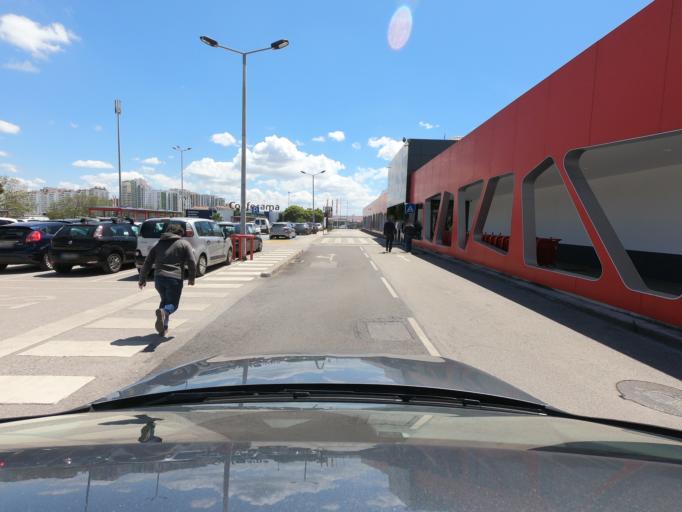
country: PT
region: Lisbon
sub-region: Amadora
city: Amadora
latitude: 38.7414
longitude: -9.2320
